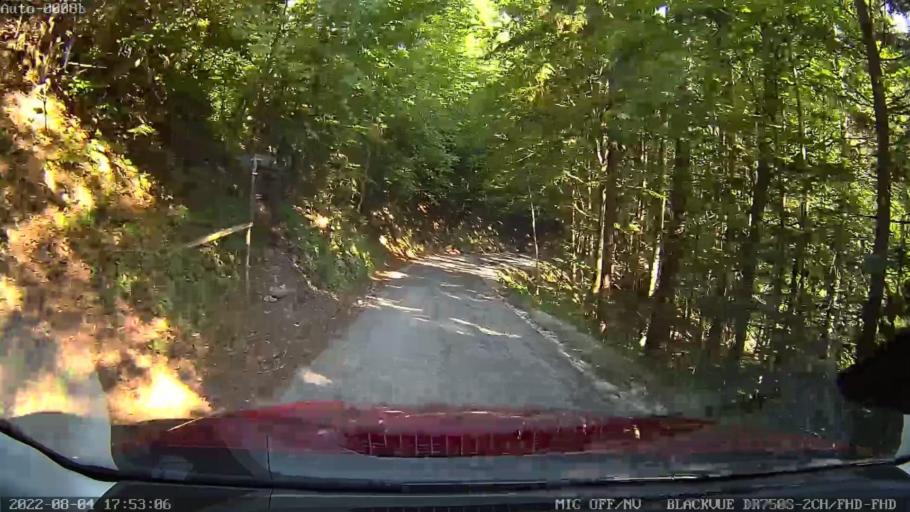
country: SI
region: Kranjska Gora
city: Kranjska Gora
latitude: 46.4869
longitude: 13.8422
